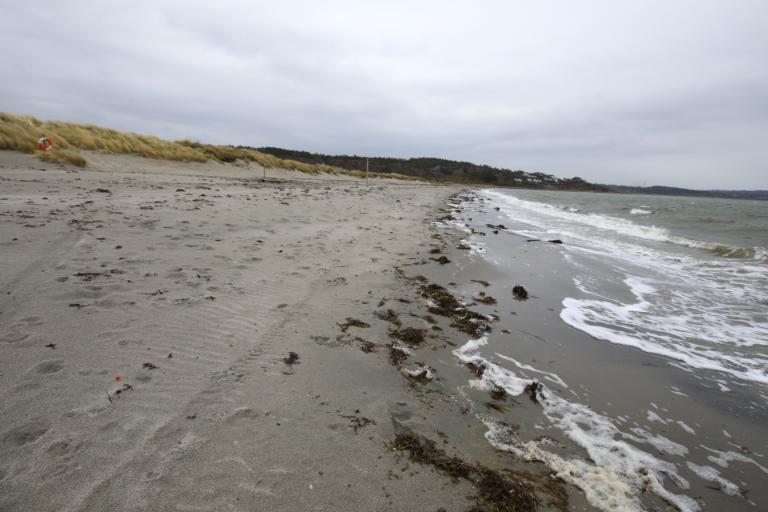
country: SE
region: Halland
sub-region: Kungsbacka Kommun
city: Frillesas
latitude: 57.2977
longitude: 12.1640
